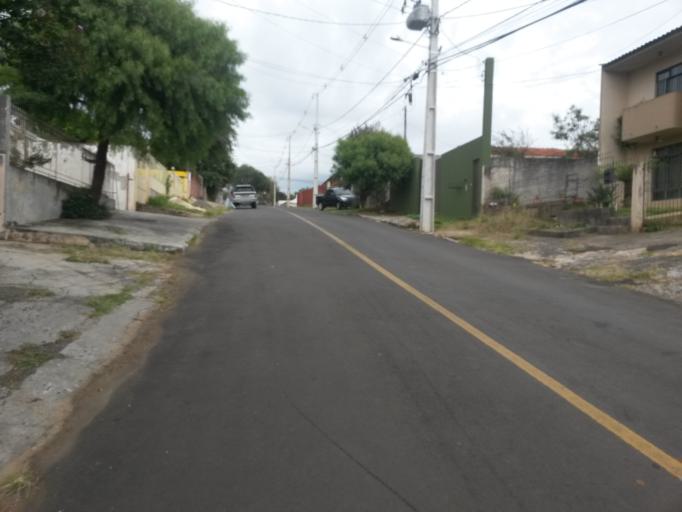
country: BR
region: Parana
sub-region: Guarapuava
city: Guarapuava
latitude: -25.3863
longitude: -51.4571
